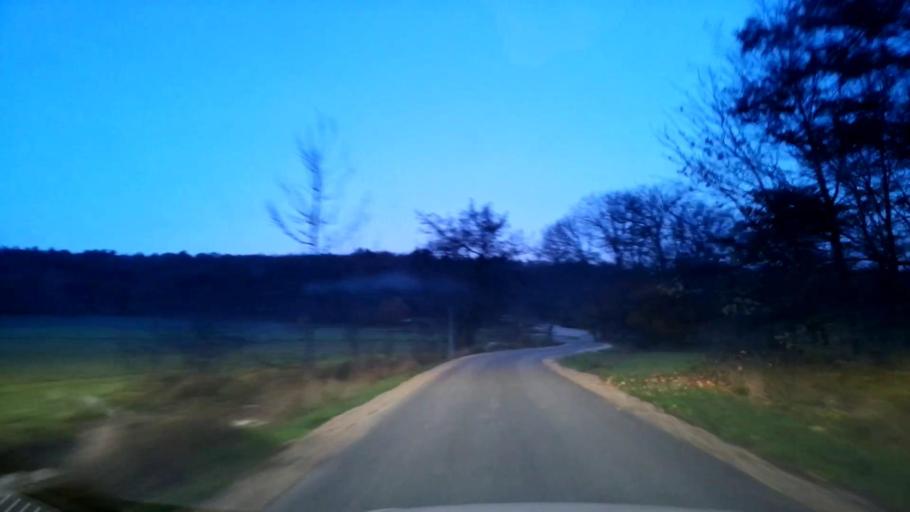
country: DE
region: Bavaria
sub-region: Upper Franconia
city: Pettstadt
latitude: 49.8500
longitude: 10.8920
